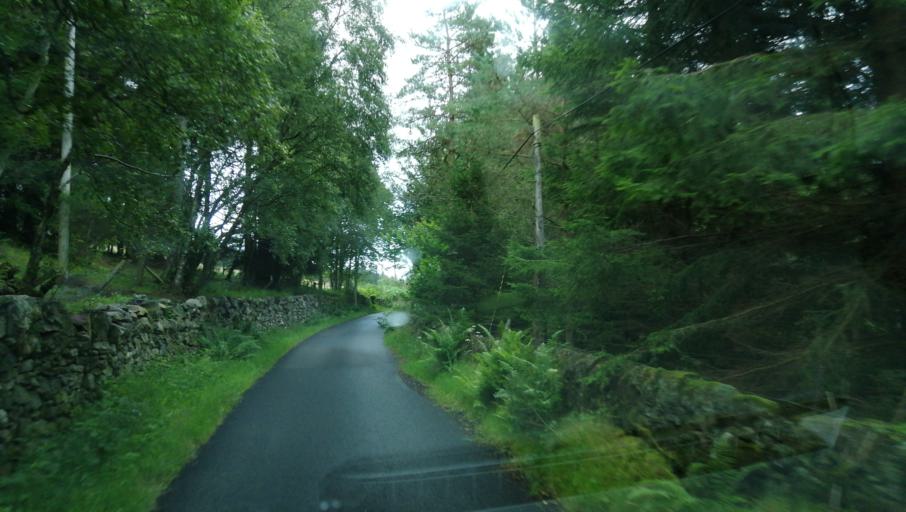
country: GB
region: Scotland
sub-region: Perth and Kinross
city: Blairgowrie
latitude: 56.6956
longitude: -3.4076
